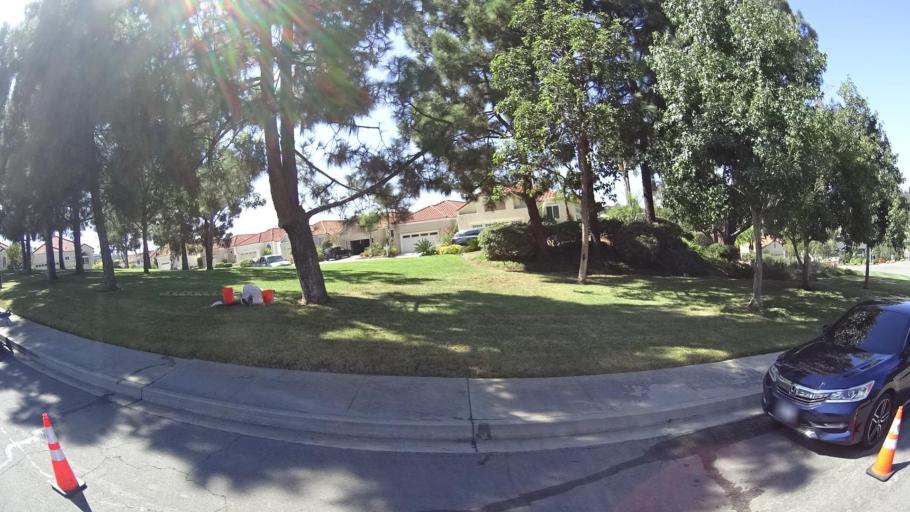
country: US
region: California
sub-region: San Diego County
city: Lake San Marcos
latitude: 33.1195
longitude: -117.2152
